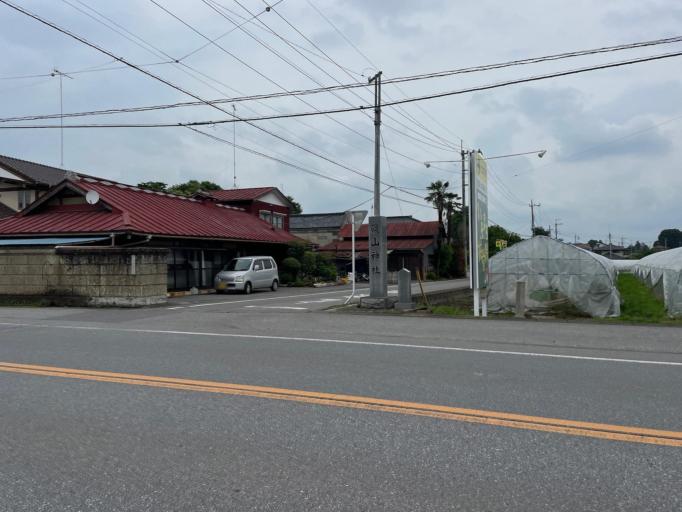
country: JP
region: Tochigi
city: Kanuma
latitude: 36.4907
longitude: 139.7496
